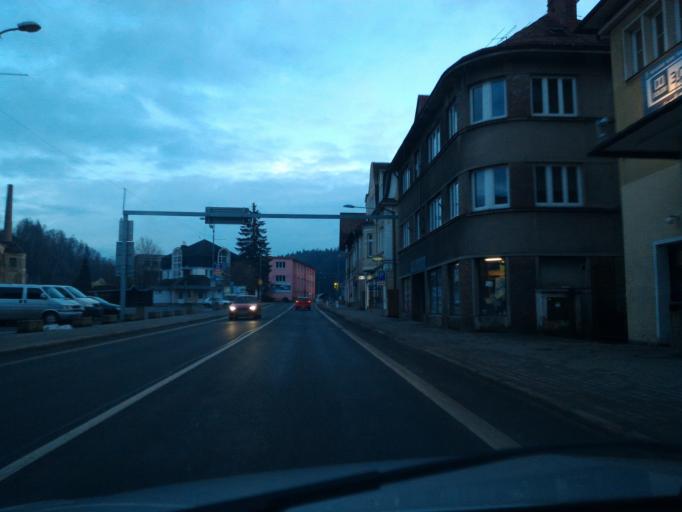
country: CZ
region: Liberecky
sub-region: Okres Jablonec nad Nisou
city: Tanvald
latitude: 50.7386
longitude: 15.3077
